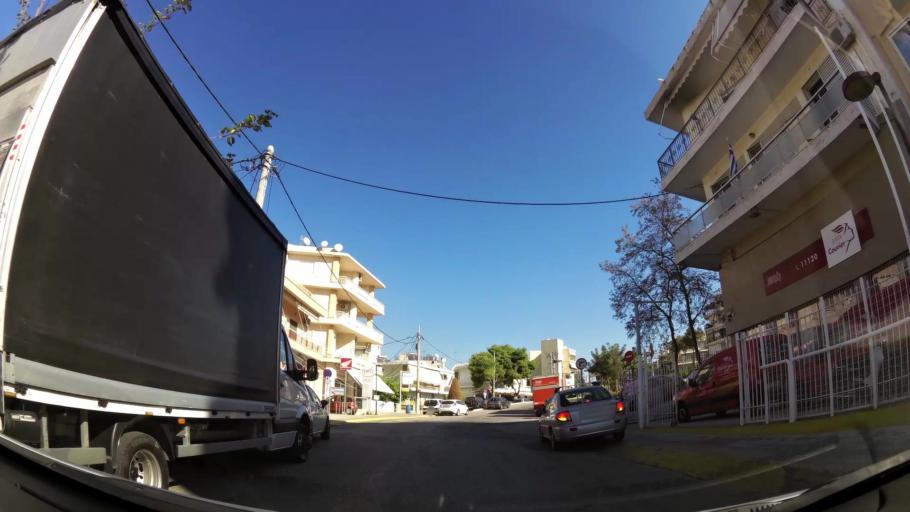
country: GR
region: Attica
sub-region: Nomarchia Athinas
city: Metamorfosi
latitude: 38.0641
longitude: 23.7641
